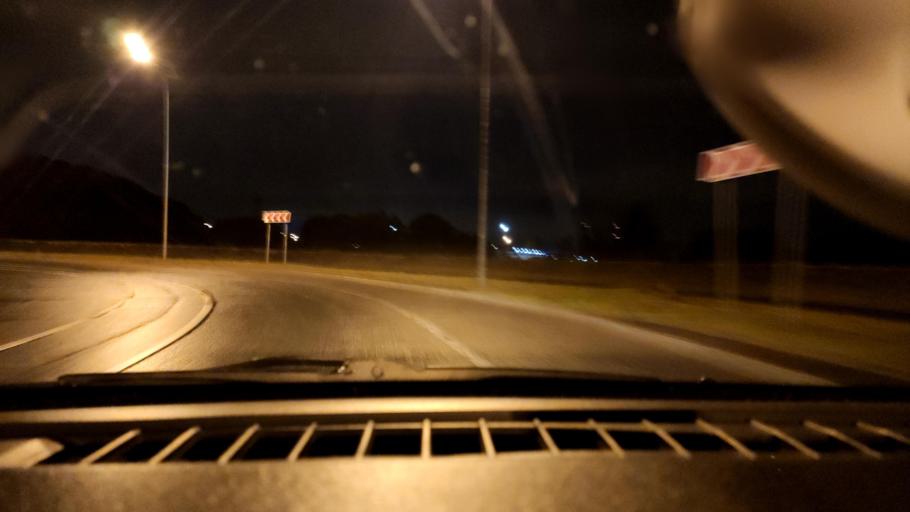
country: RU
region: Samara
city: Smyshlyayevka
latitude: 53.1847
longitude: 50.3048
